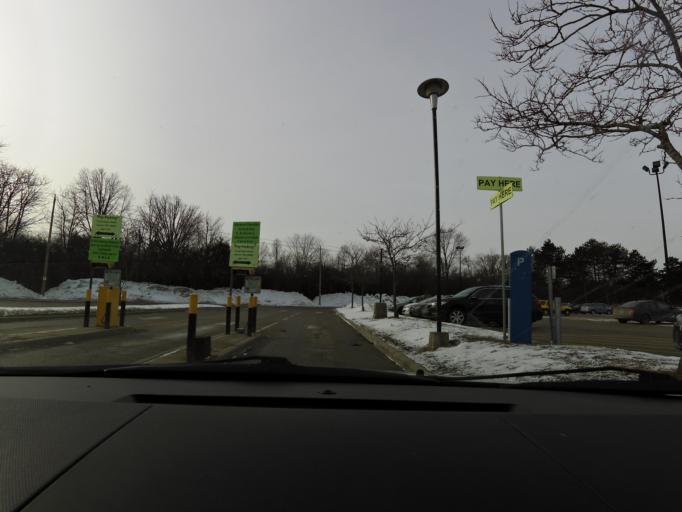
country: CA
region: Ontario
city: Waterloo
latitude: 43.4672
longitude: -80.5385
